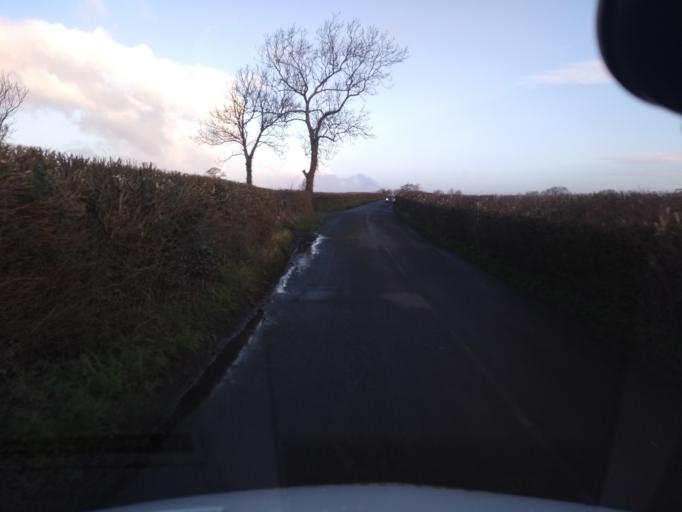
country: GB
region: England
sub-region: Somerset
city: Wedmore
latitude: 51.2323
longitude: -2.8154
